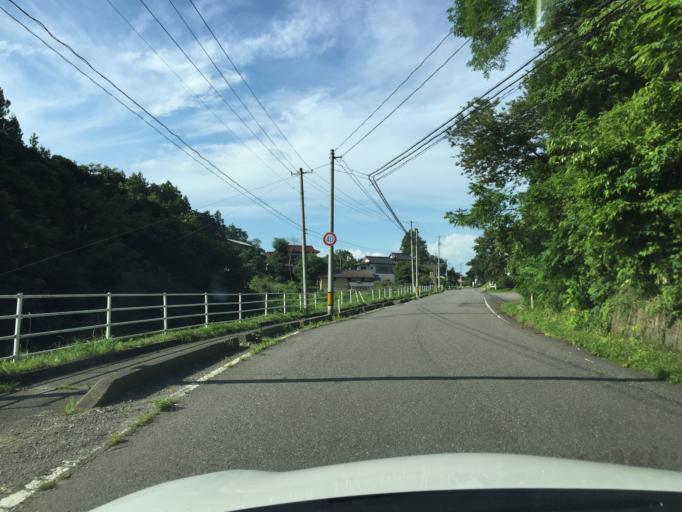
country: JP
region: Fukushima
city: Sukagawa
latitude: 37.3194
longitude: 140.4857
